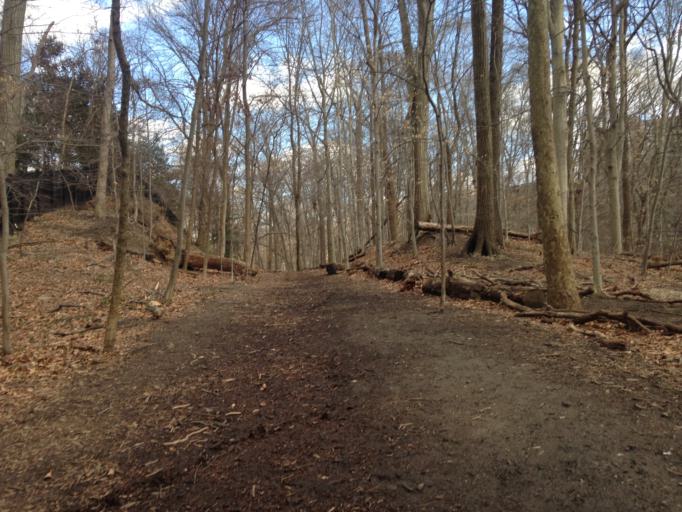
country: US
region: Maryland
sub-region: Montgomery County
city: Chevy Chase Village
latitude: 38.9472
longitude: -77.0634
